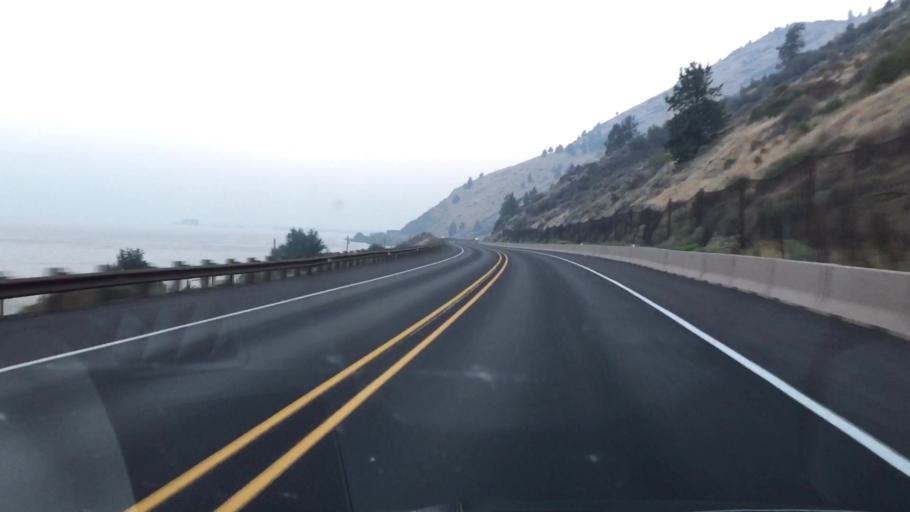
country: US
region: Oregon
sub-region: Klamath County
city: Klamath Falls
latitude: 42.4252
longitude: -121.8515
